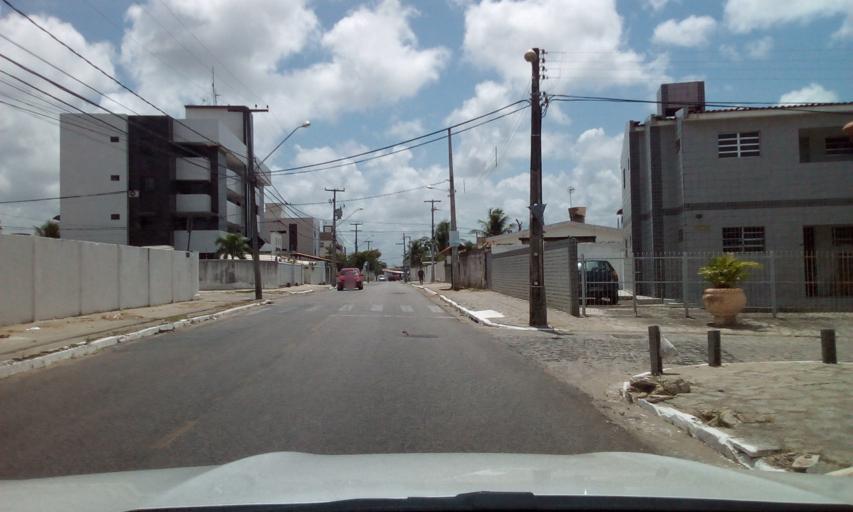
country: BR
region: Paraiba
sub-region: Joao Pessoa
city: Joao Pessoa
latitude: -7.1830
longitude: -34.8664
